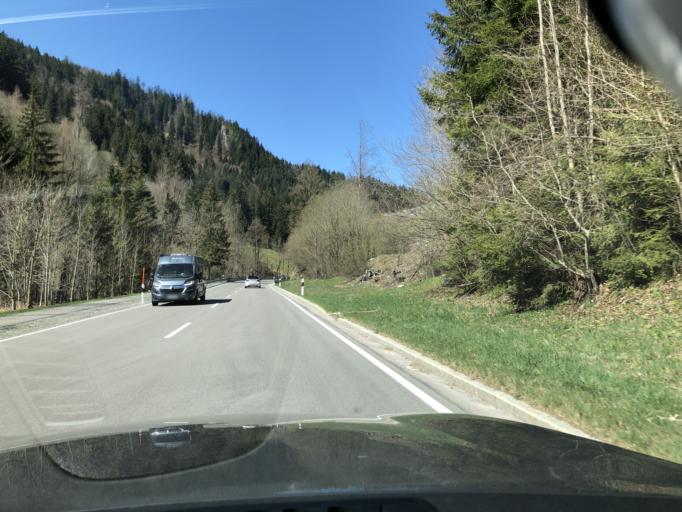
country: DE
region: Bavaria
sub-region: Swabia
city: Wertach
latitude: 47.5825
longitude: 10.4158
